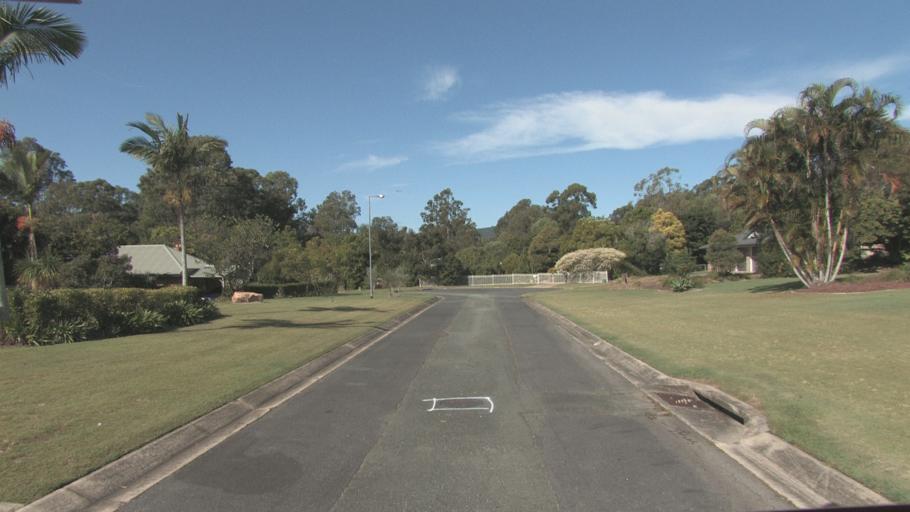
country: AU
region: Queensland
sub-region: Logan
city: Windaroo
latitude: -27.7608
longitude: 153.1832
